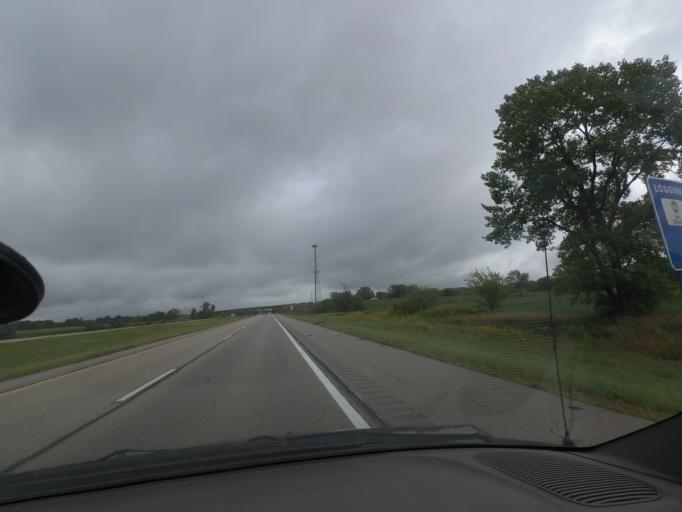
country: US
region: Illinois
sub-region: Piatt County
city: Monticello
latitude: 40.0411
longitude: -88.5875
